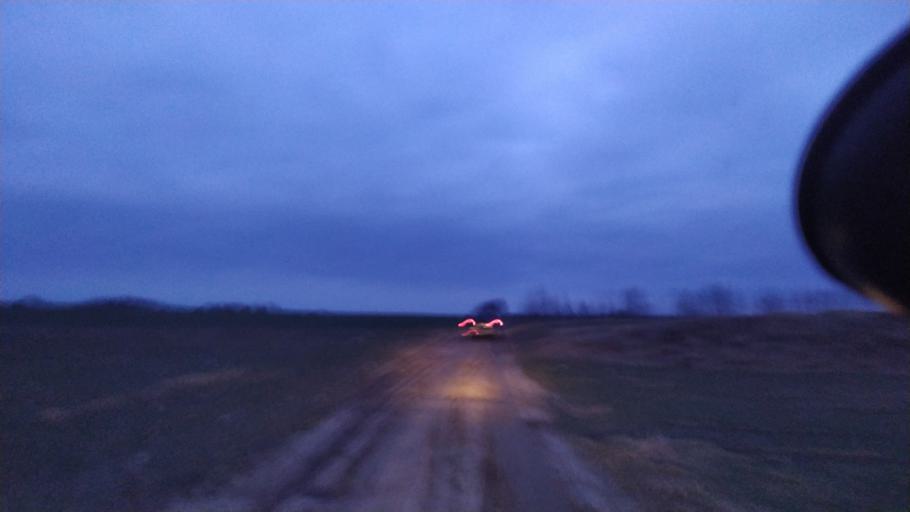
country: PL
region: Lublin Voivodeship
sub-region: Powiat lubartowski
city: Kamionka
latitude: 51.3922
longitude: 22.4277
